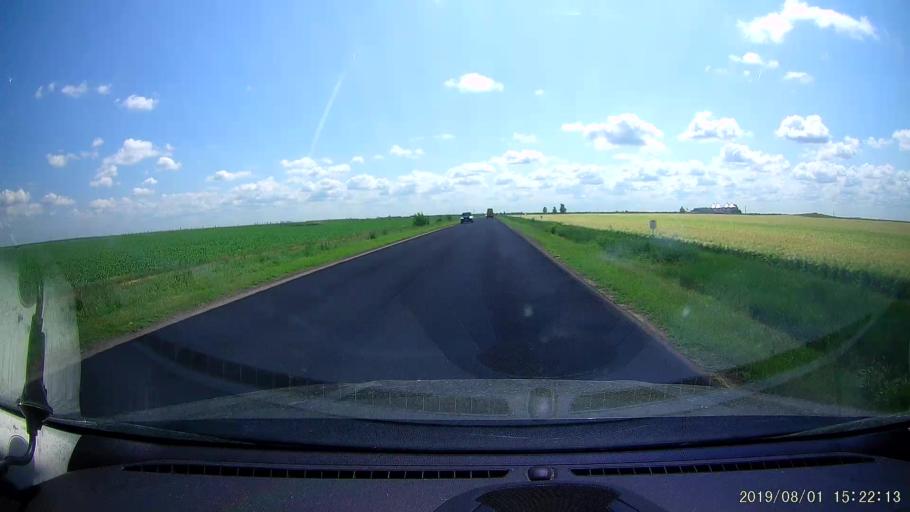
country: RO
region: Braila
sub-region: Comuna Viziru
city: Lanurile
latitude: 45.0571
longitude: 27.7804
